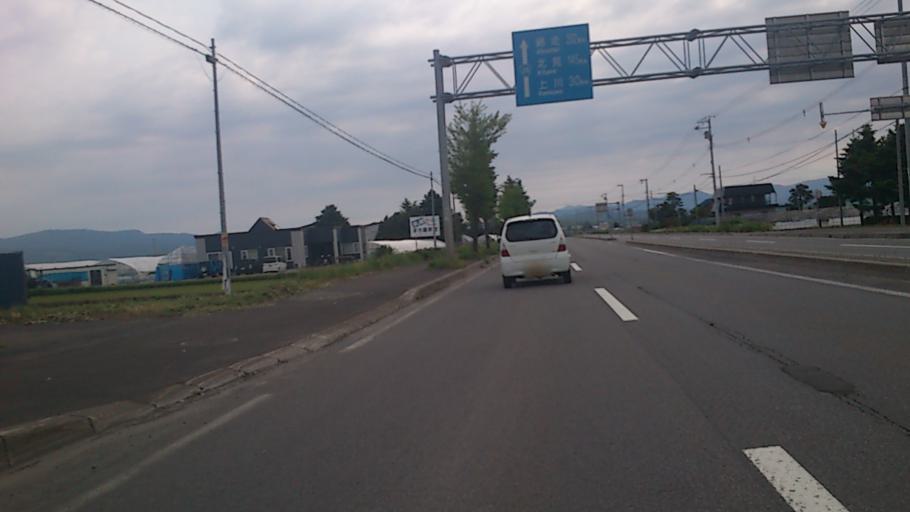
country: JP
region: Hokkaido
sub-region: Asahikawa-shi
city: Asahikawa
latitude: 43.8456
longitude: 142.4900
